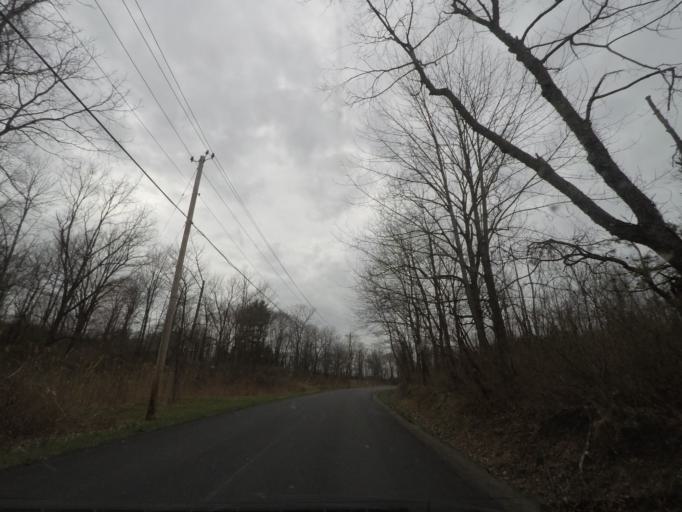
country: US
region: New York
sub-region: Rensselaer County
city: Castleton-on-Hudson
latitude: 42.5544
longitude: -73.7778
